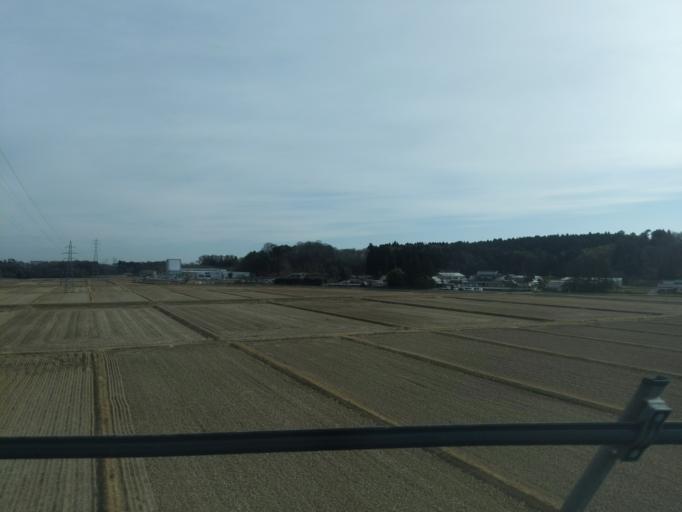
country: JP
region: Iwate
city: Ichinoseki
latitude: 38.7399
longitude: 141.0667
